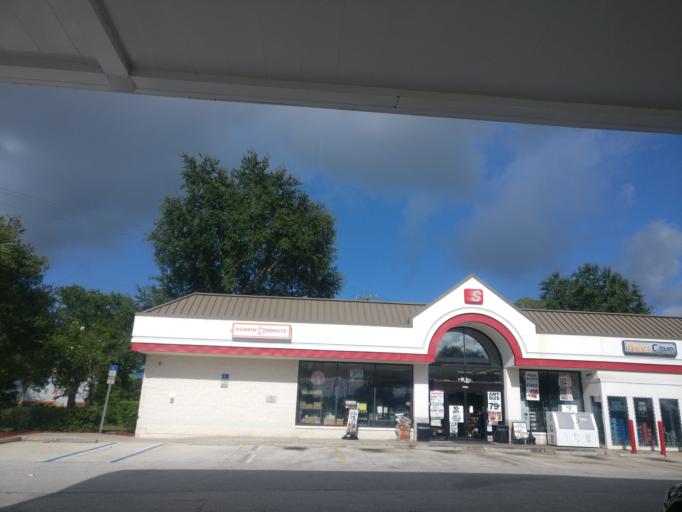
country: US
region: Florida
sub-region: Volusia County
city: Daytona Beach
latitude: 29.1746
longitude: -81.0824
